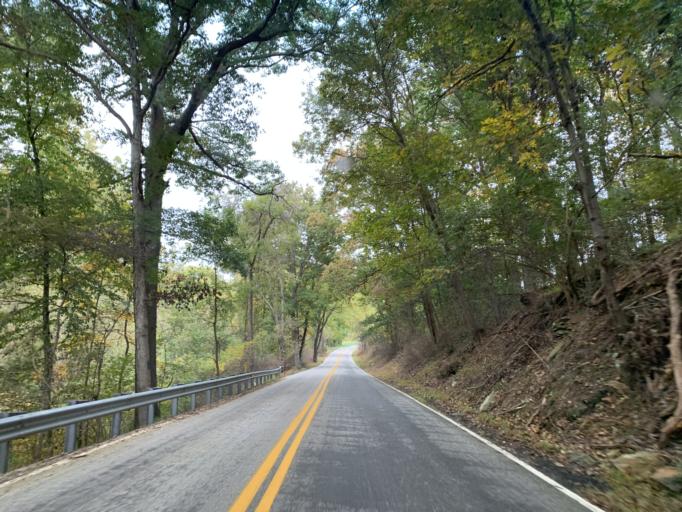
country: US
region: Pennsylvania
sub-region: York County
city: Susquehanna Trails
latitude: 39.7750
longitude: -76.4230
